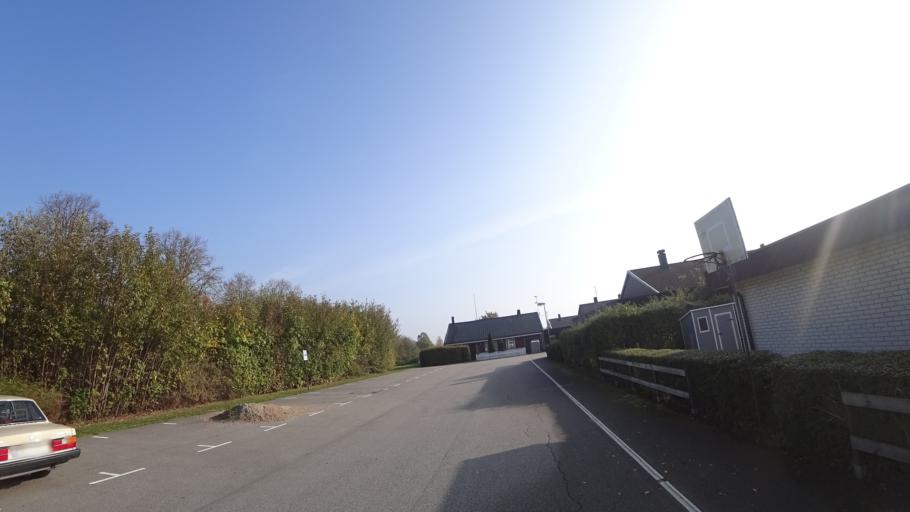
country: SE
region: Skane
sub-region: Staffanstorps Kommun
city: Staffanstorp
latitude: 55.6538
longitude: 13.2073
